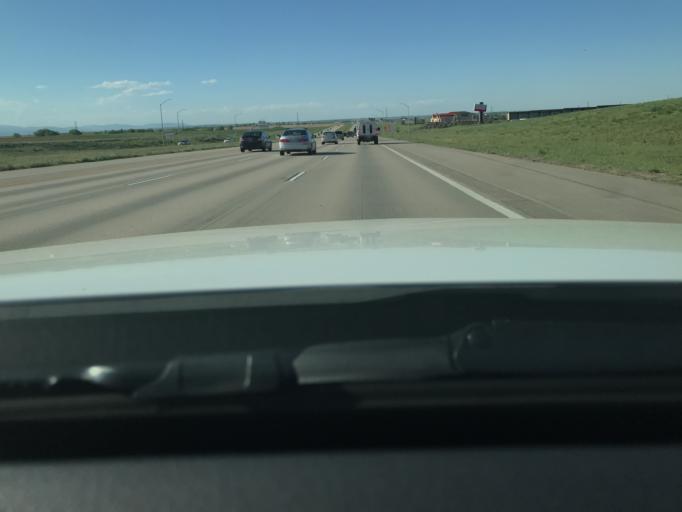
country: US
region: Colorado
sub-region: Weld County
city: Dacono
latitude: 40.0453
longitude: -104.9796
